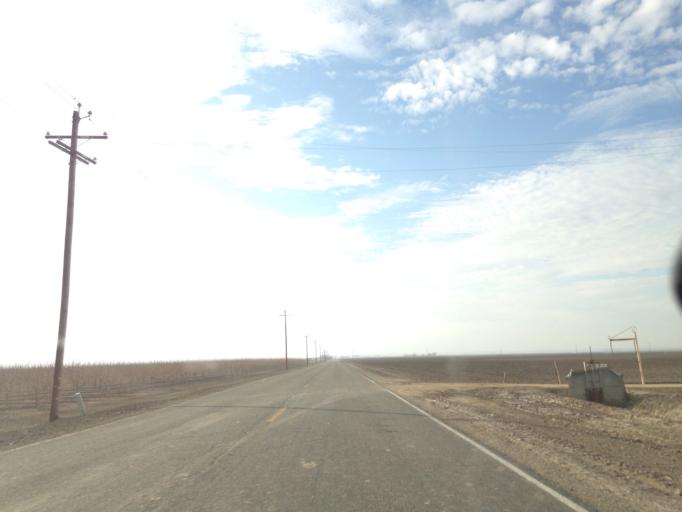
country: US
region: California
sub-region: Kern County
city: Buttonwillow
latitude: 35.4418
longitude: -119.5394
